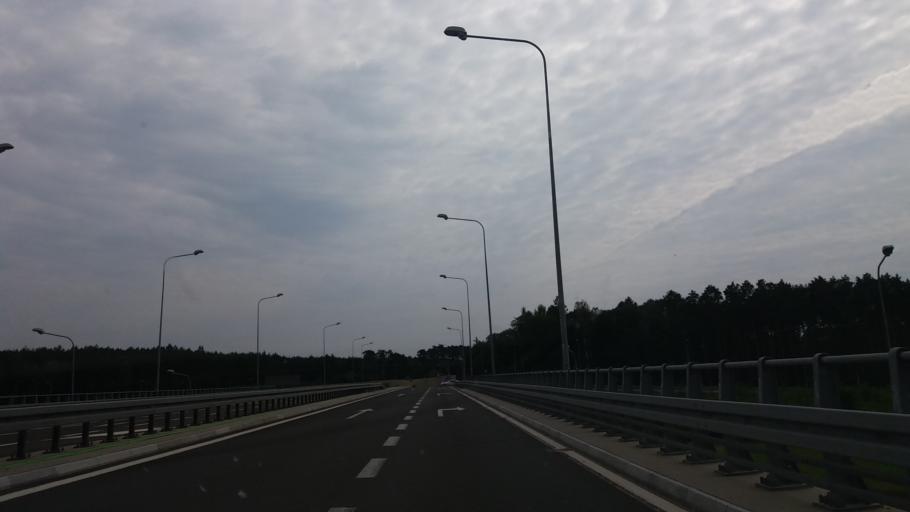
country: PL
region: Lubusz
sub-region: Powiat miedzyrzecki
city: Skwierzyna
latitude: 52.5609
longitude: 15.5246
